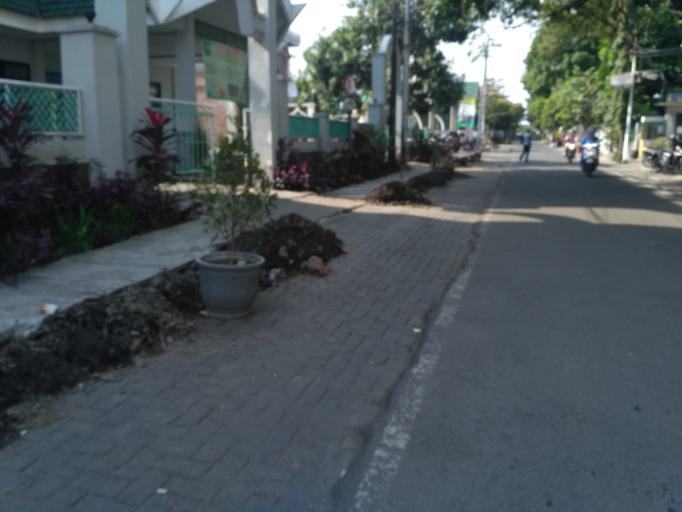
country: ID
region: East Java
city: Malang
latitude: -7.9362
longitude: 112.6064
